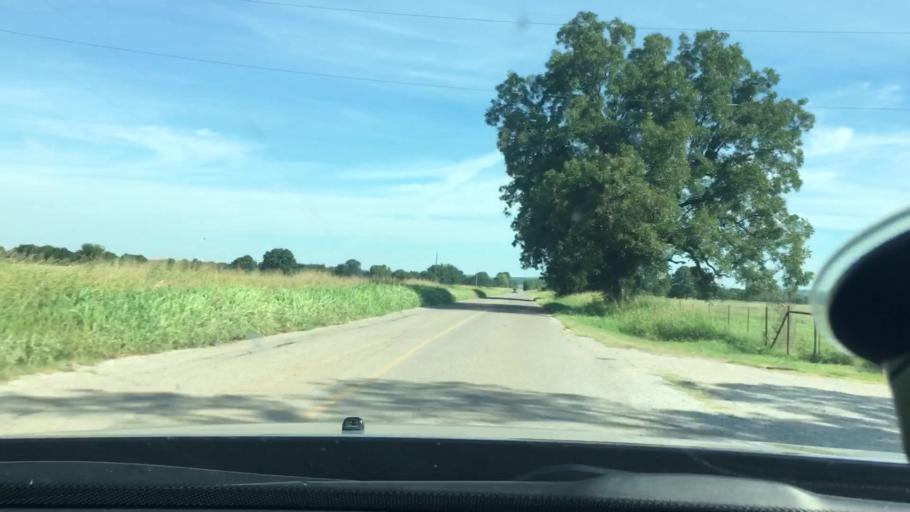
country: US
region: Oklahoma
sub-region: Carter County
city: Lone Grove
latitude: 34.2962
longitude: -97.2824
